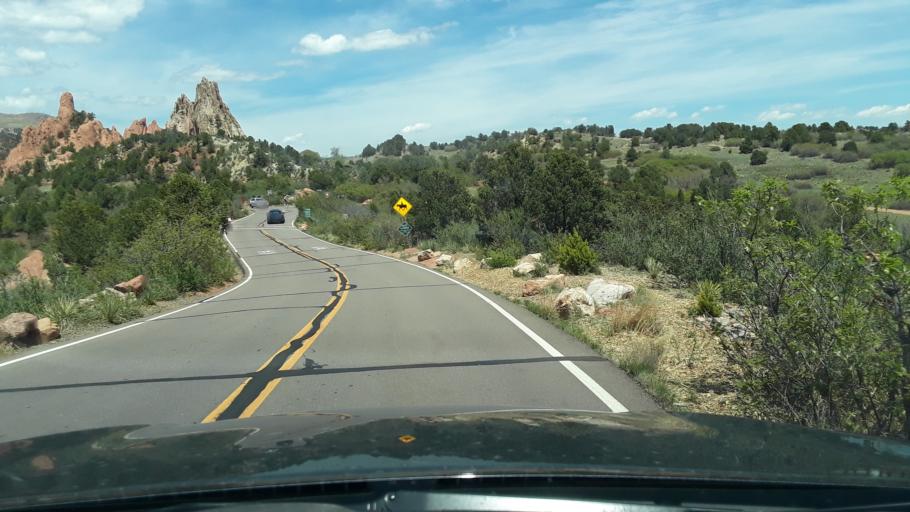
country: US
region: Colorado
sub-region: El Paso County
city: Manitou Springs
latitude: 38.8667
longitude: -104.8790
